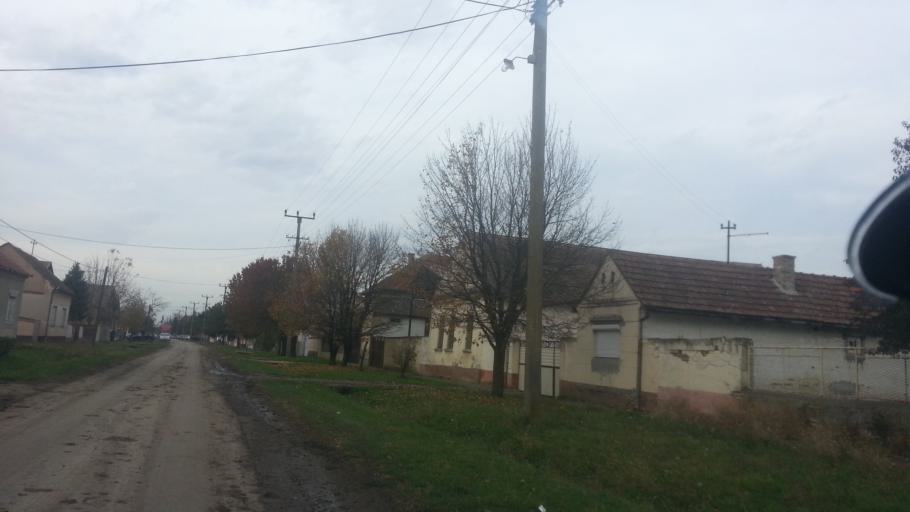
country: RS
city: Putinci
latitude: 44.9626
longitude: 19.9807
